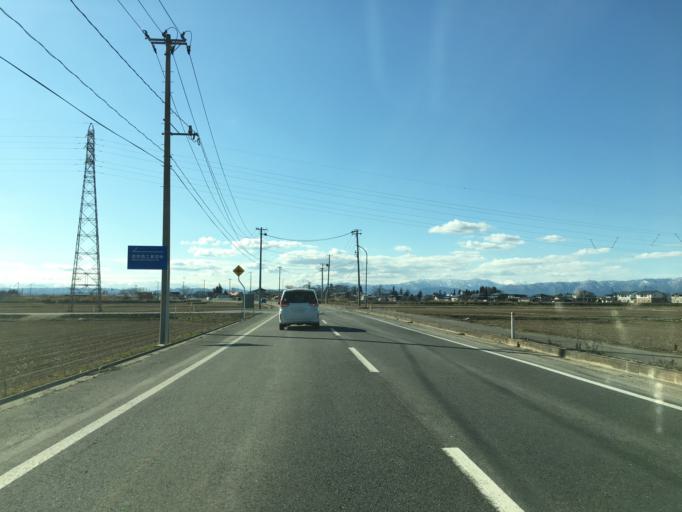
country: JP
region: Yamagata
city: Takahata
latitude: 38.0072
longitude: 140.1446
